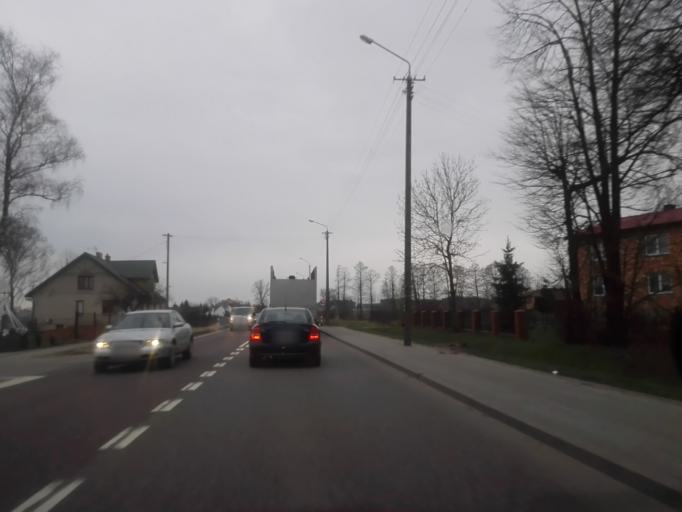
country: PL
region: Podlasie
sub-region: Powiat grajewski
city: Grajewo
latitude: 53.6232
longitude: 22.4023
